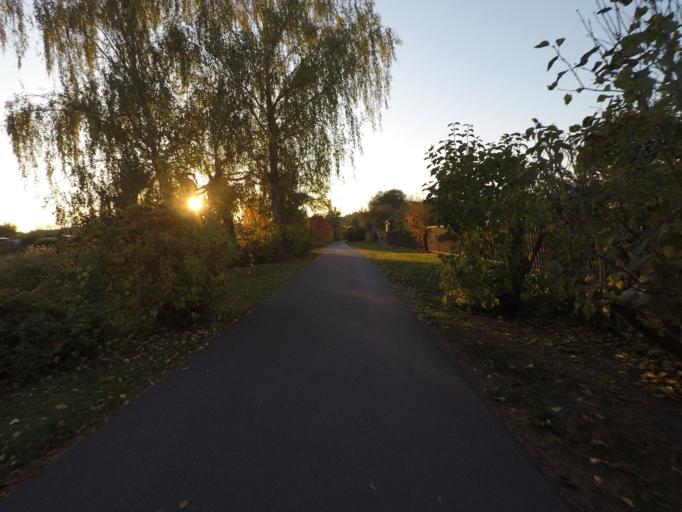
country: DE
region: Brandenburg
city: Melchow
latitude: 52.8458
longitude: 13.7172
